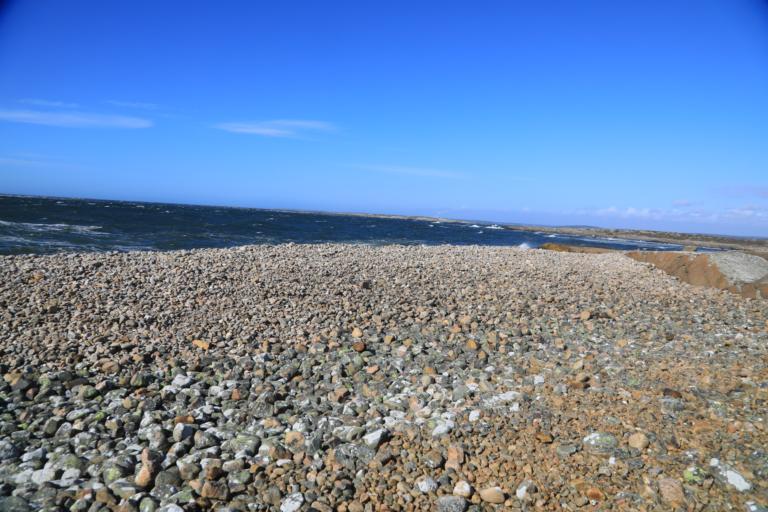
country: SE
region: Halland
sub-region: Varbergs Kommun
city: Varberg
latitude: 57.1166
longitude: 12.1904
